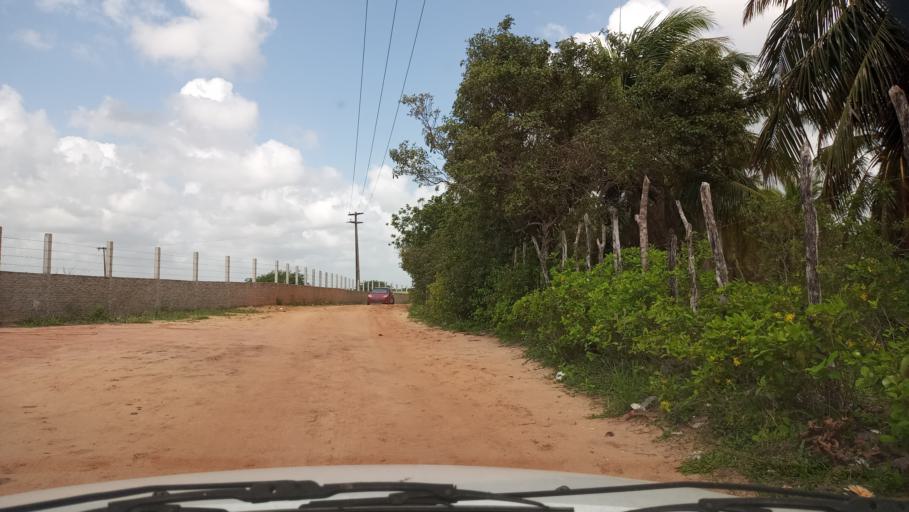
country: BR
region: Rio Grande do Norte
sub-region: Ares
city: Ares
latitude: -6.2368
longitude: -35.1382
